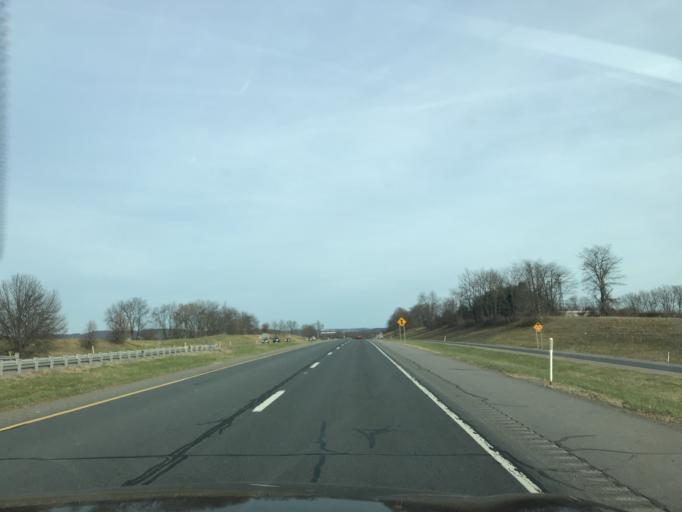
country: US
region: Pennsylvania
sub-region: Lycoming County
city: Muncy
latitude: 41.2375
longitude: -76.8090
